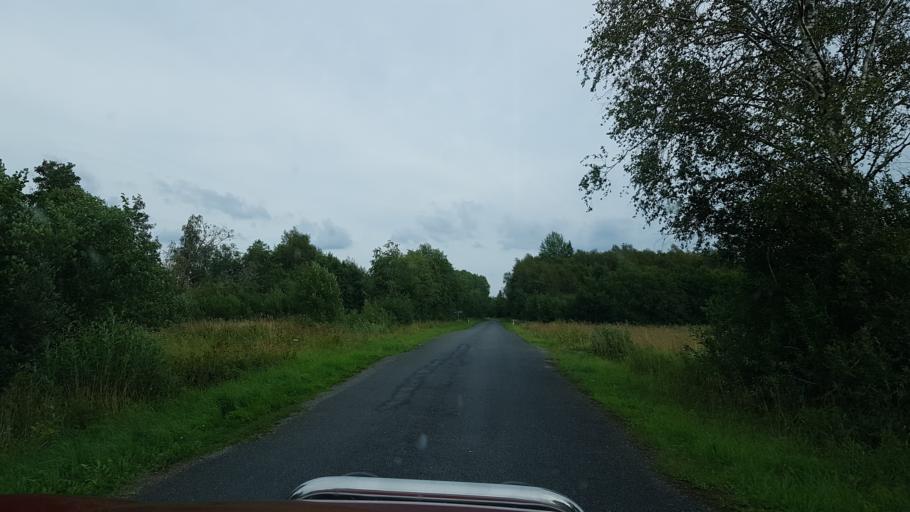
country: EE
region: Laeaene
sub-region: Ridala Parish
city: Uuemoisa
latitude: 58.9829
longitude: 23.8164
